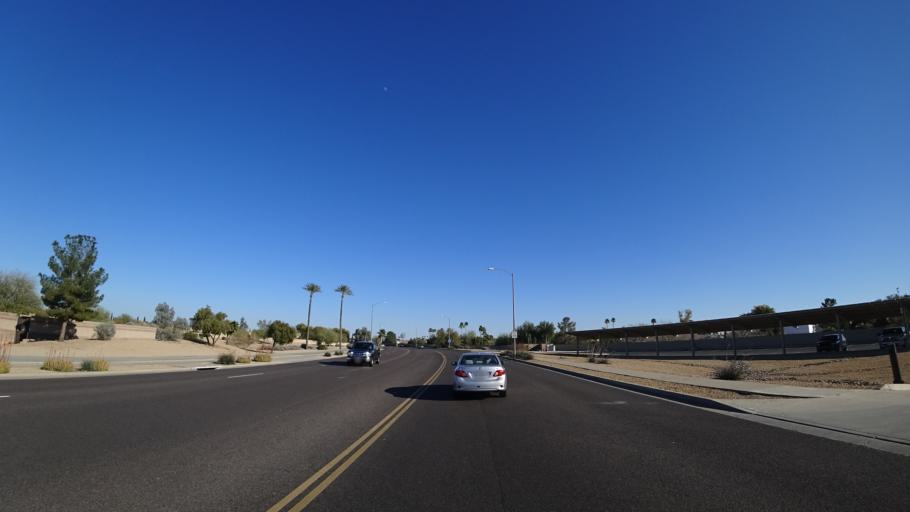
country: US
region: Arizona
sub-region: Maricopa County
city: Sun City West
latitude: 33.6826
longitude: -112.3538
